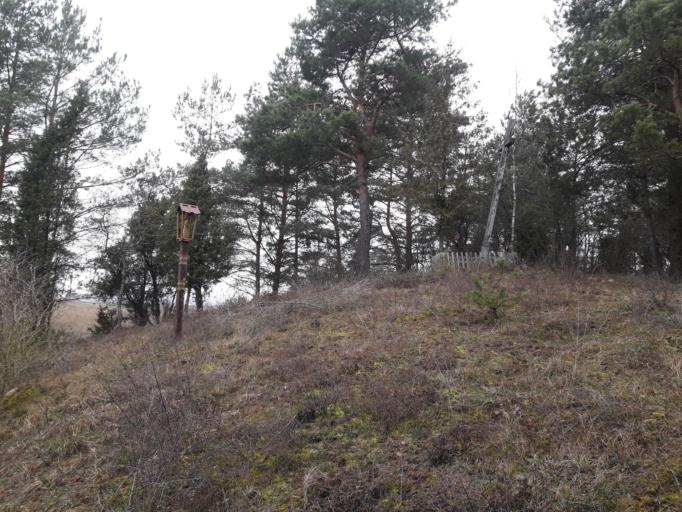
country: LT
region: Alytaus apskritis
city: Druskininkai
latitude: 54.1574
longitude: 24.0660
